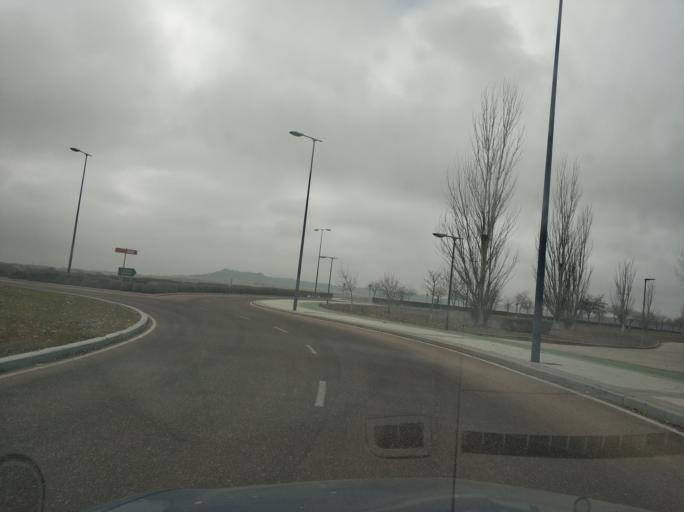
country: ES
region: Castille and Leon
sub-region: Provincia de Valladolid
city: Arroyo
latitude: 41.6130
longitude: -4.8001
